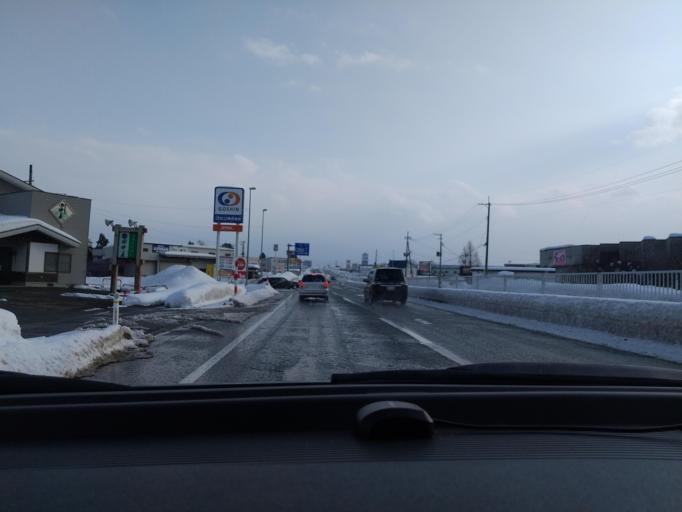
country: JP
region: Akita
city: Omagari
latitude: 39.4668
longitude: 140.4890
